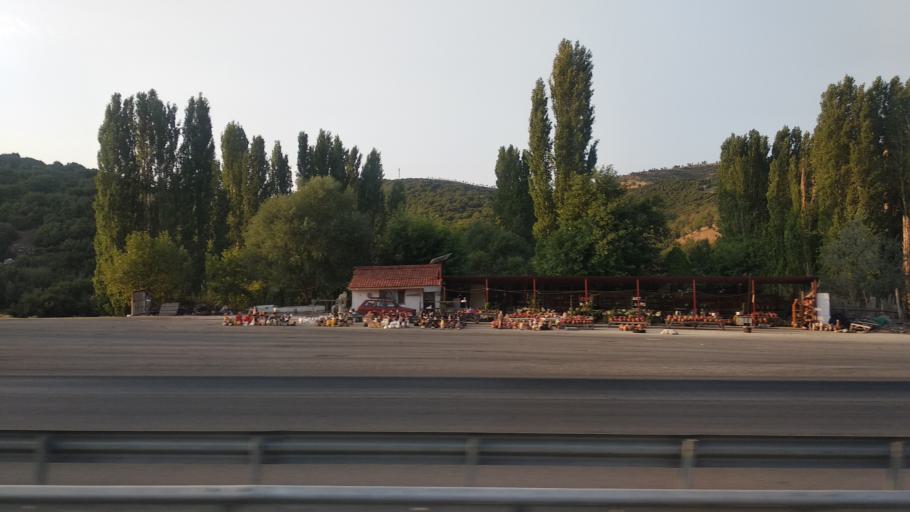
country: TR
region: Manisa
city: Menye
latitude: 38.5533
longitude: 28.4690
